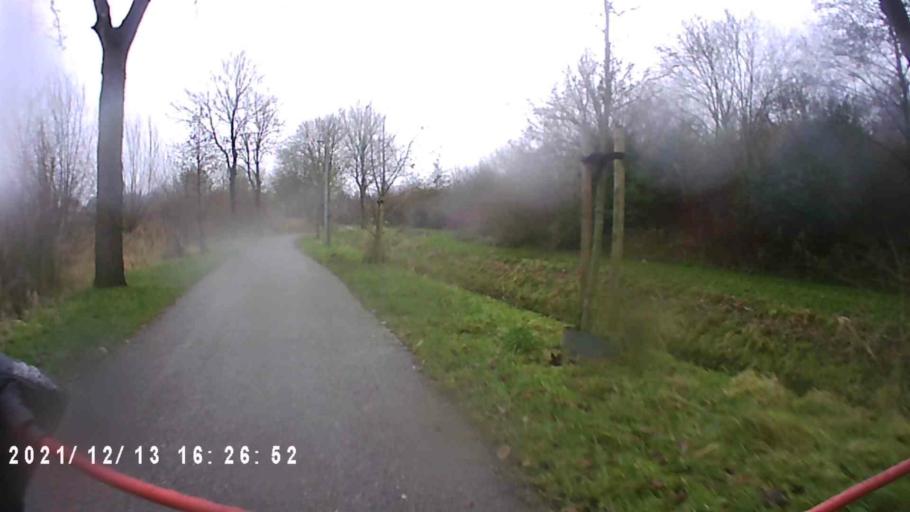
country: NL
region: Groningen
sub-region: Gemeente Delfzijl
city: Delfzijl
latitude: 53.3282
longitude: 6.8887
